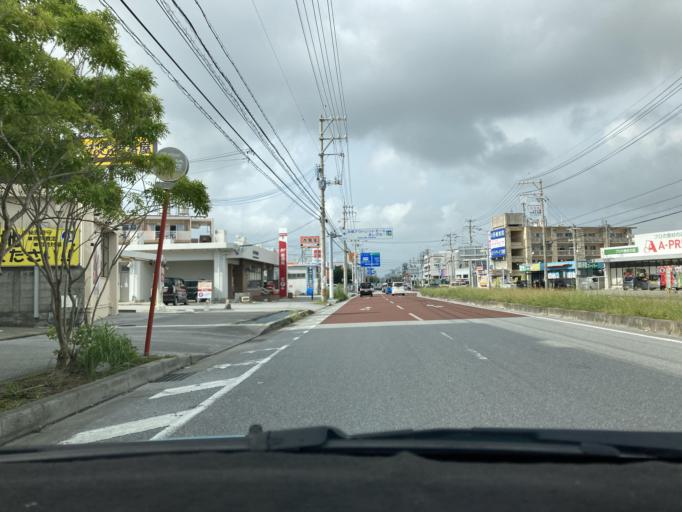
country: JP
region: Okinawa
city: Itoman
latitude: 26.1494
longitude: 127.6727
